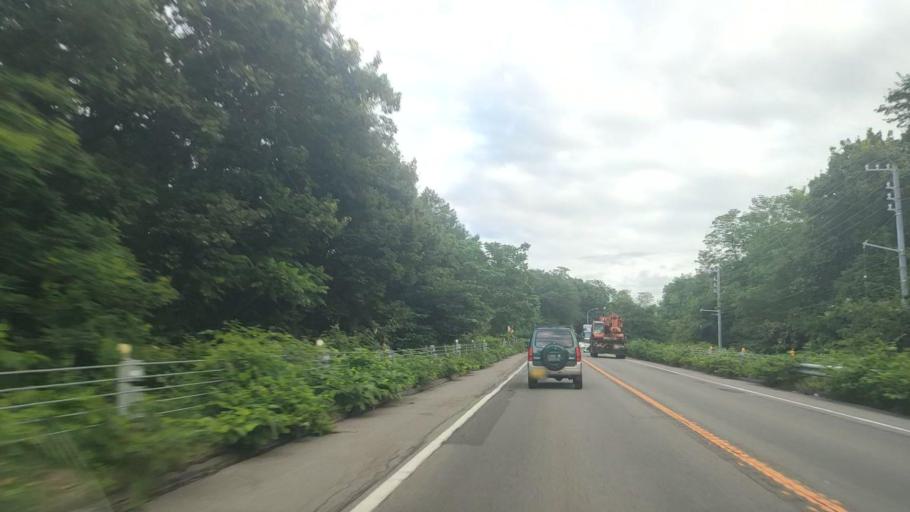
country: JP
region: Hokkaido
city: Nanae
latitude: 42.0732
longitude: 140.6019
